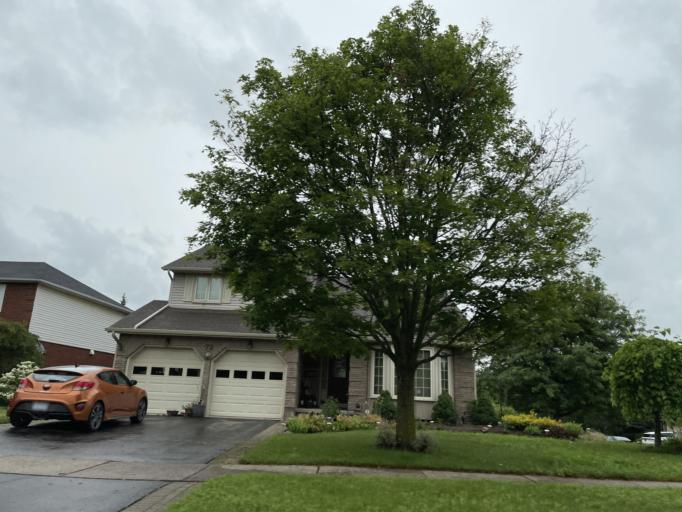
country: CA
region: Ontario
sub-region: Wellington County
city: Guelph
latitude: 43.5027
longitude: -80.2392
